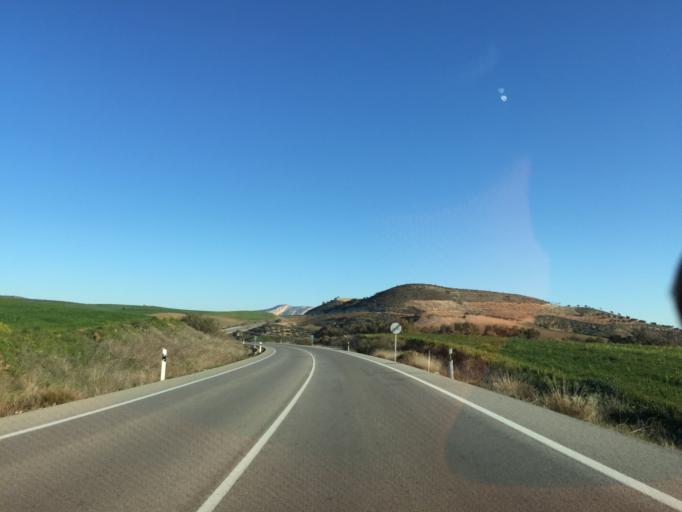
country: ES
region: Andalusia
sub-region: Provincia de Malaga
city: Ardales
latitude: 36.9031
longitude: -4.8404
